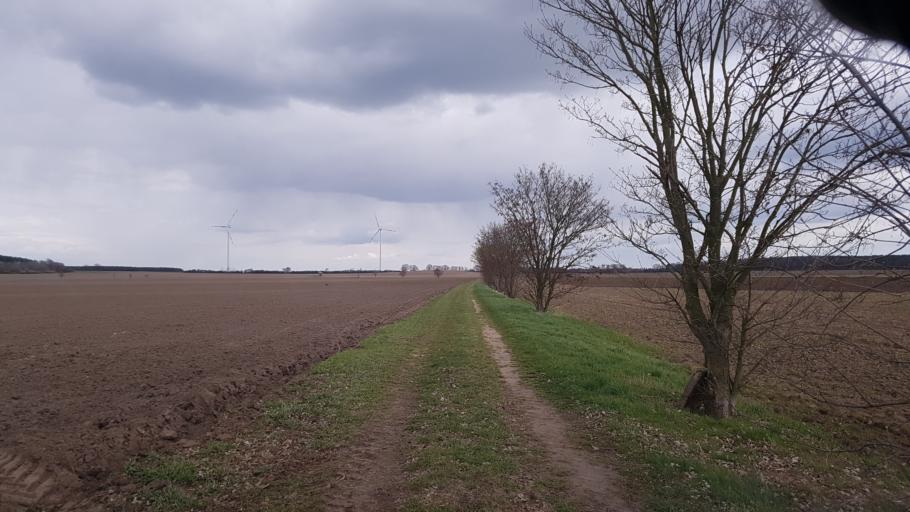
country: DE
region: Brandenburg
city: Hohenbucko
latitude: 51.6967
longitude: 13.4770
